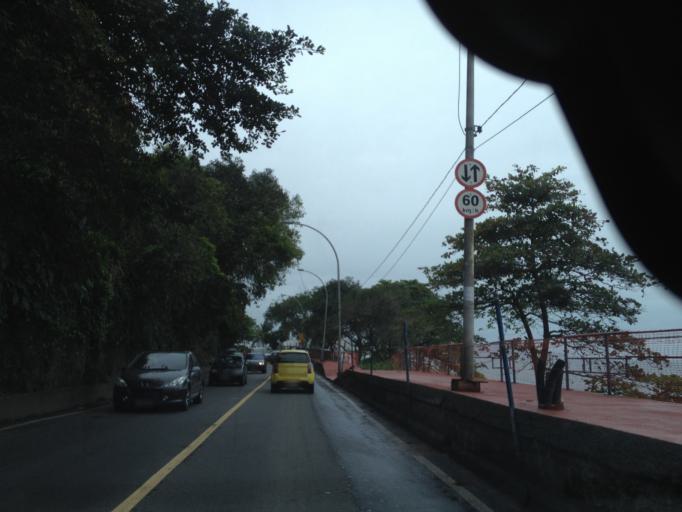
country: BR
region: Rio de Janeiro
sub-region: Rio De Janeiro
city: Rio de Janeiro
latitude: -22.9969
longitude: -43.2368
